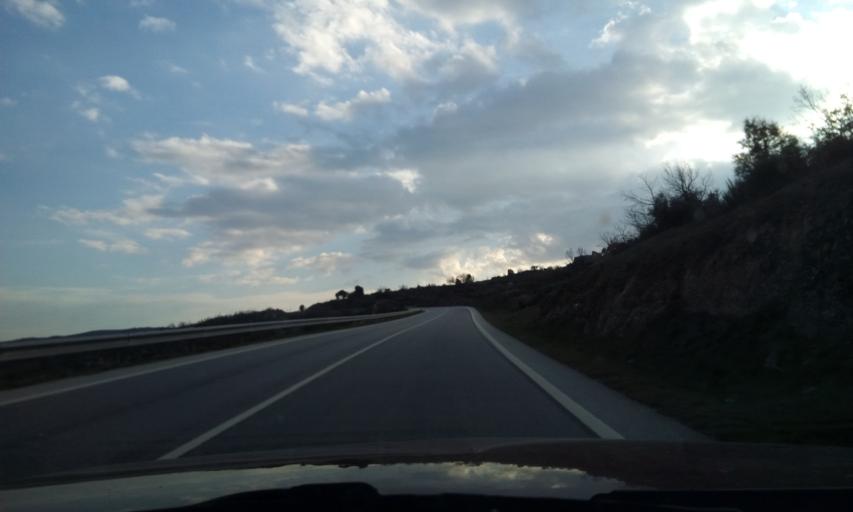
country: ES
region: Castille and Leon
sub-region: Provincia de Salamanca
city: Aldea del Obispo
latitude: 40.6978
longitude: -6.9338
